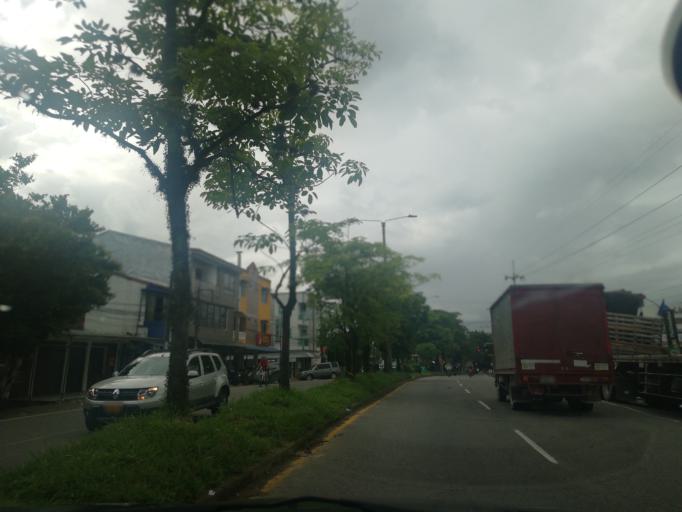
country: CO
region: Meta
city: Acacias
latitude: 3.9885
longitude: -73.7660
